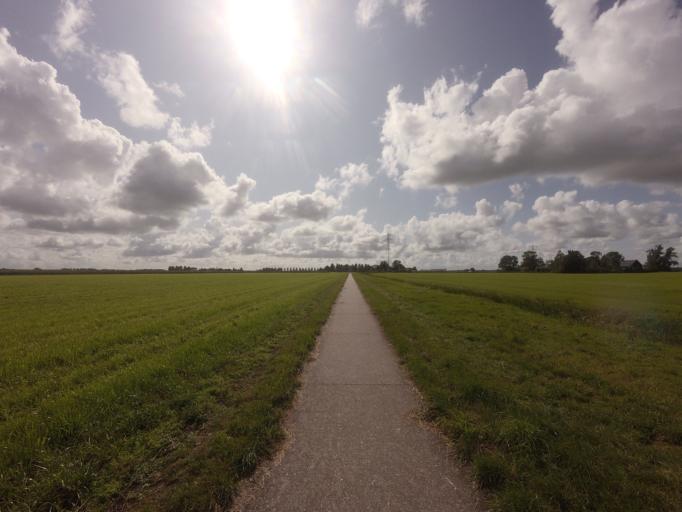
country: NL
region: Friesland
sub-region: Sudwest Fryslan
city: Sneek
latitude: 53.0645
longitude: 5.6357
